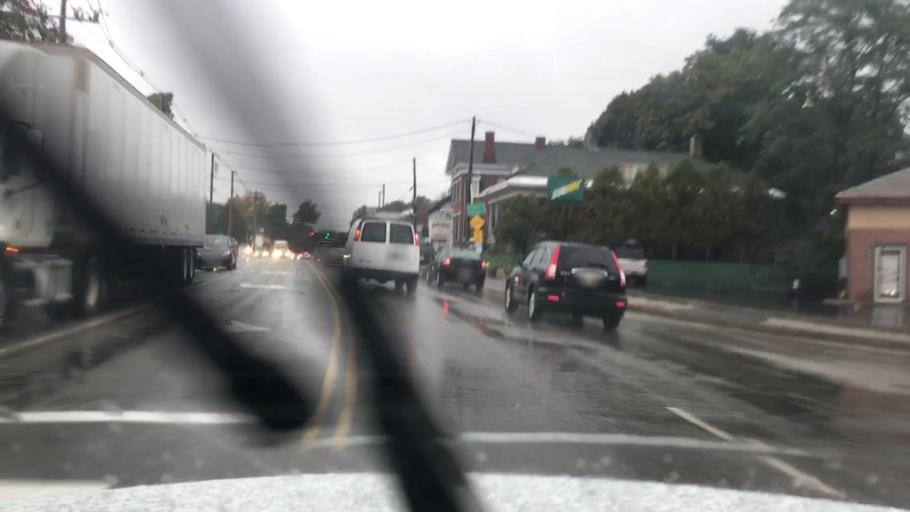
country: US
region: Maine
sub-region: Cumberland County
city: Portland
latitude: 43.6887
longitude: -70.2939
